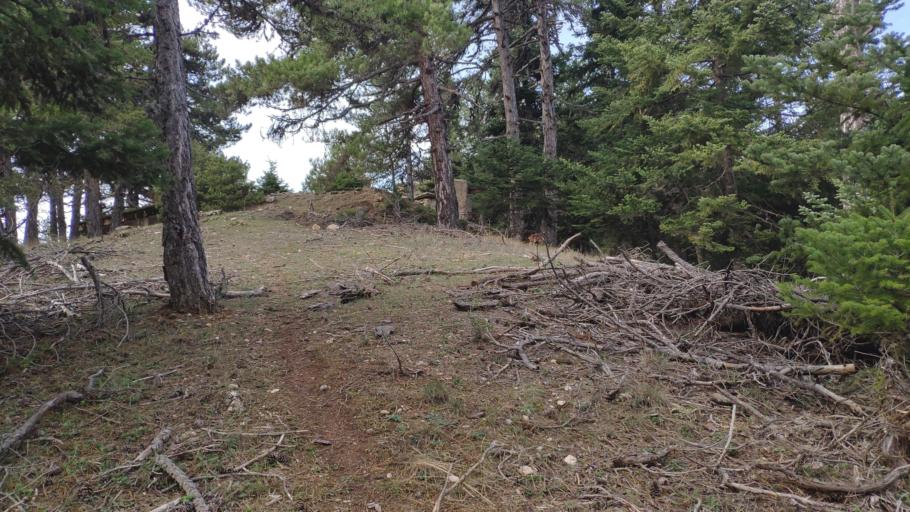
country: GR
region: West Greece
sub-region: Nomos Achaias
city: Aiyira
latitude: 38.0303
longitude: 22.3730
